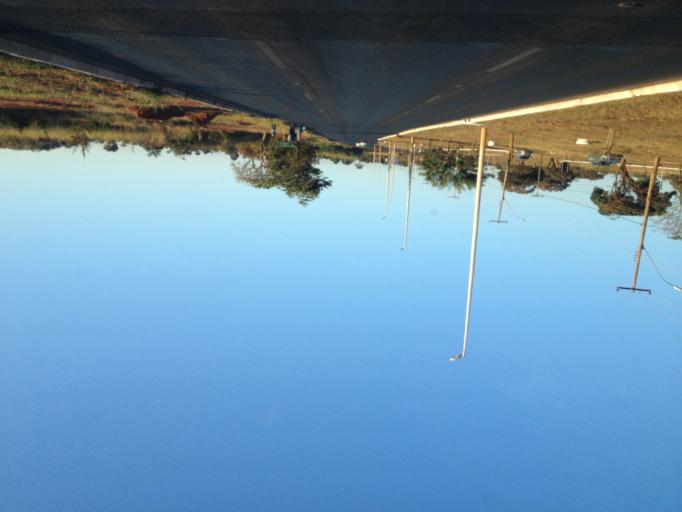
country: BR
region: Federal District
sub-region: Brasilia
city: Brasilia
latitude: -15.7657
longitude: -47.9147
